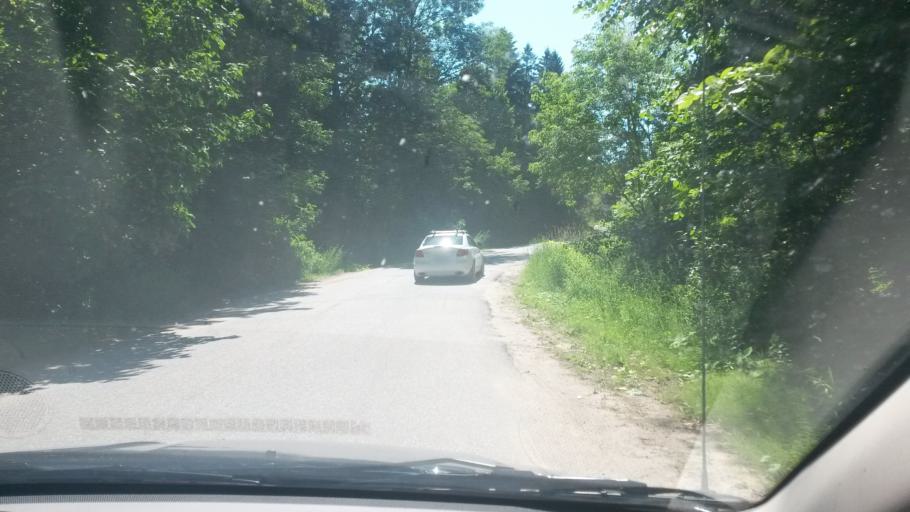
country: CA
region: Ontario
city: Barrie
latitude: 44.5519
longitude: -79.6770
